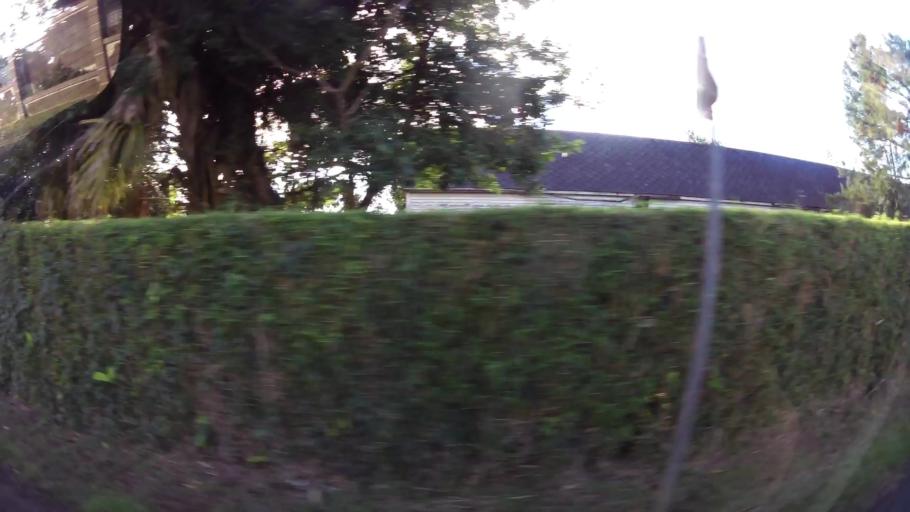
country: MU
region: Plaines Wilhems
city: Vacoas
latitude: -20.2914
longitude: 57.4954
